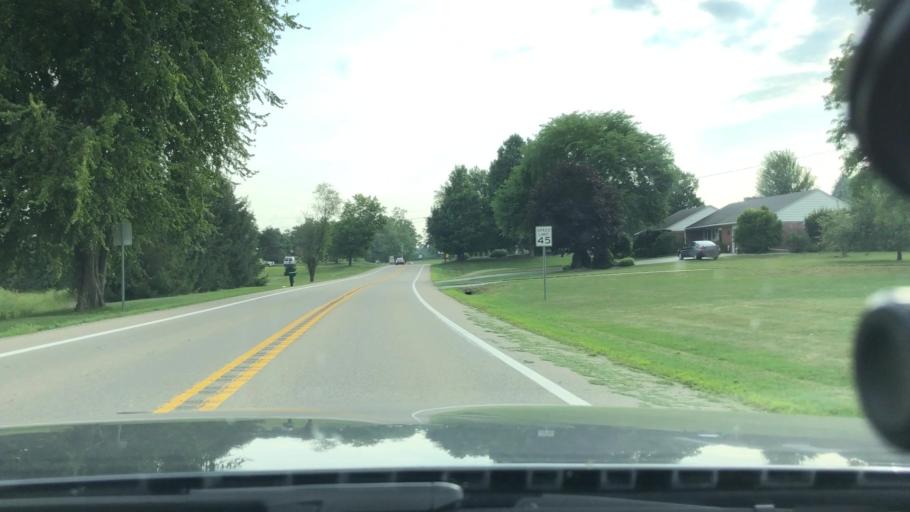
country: US
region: Michigan
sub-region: Washtenaw County
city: Manchester
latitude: 42.1639
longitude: -84.0357
